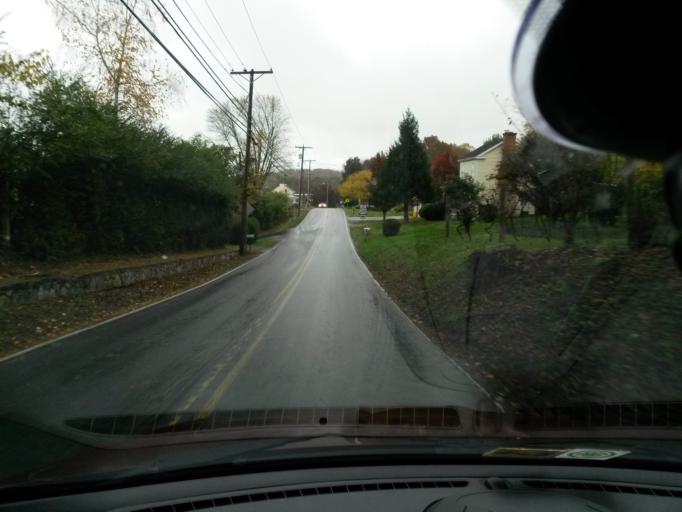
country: US
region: Virginia
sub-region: Botetourt County
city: Fincastle
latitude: 37.4997
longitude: -79.8725
